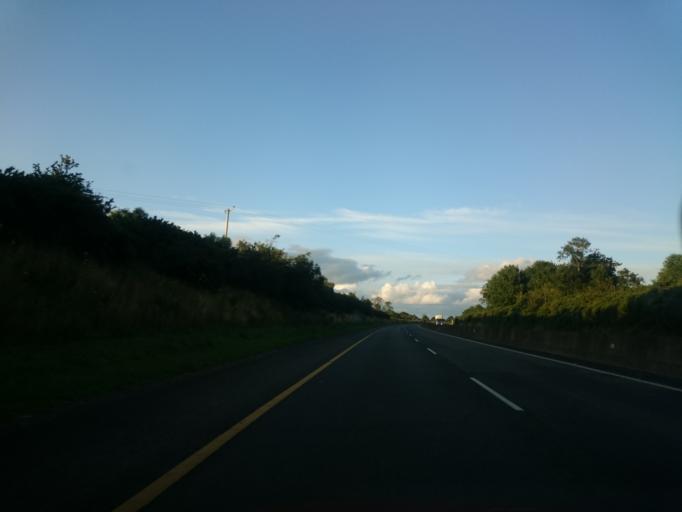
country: IE
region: Leinster
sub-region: Loch Garman
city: Gorey
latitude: 52.6429
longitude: -6.3364
